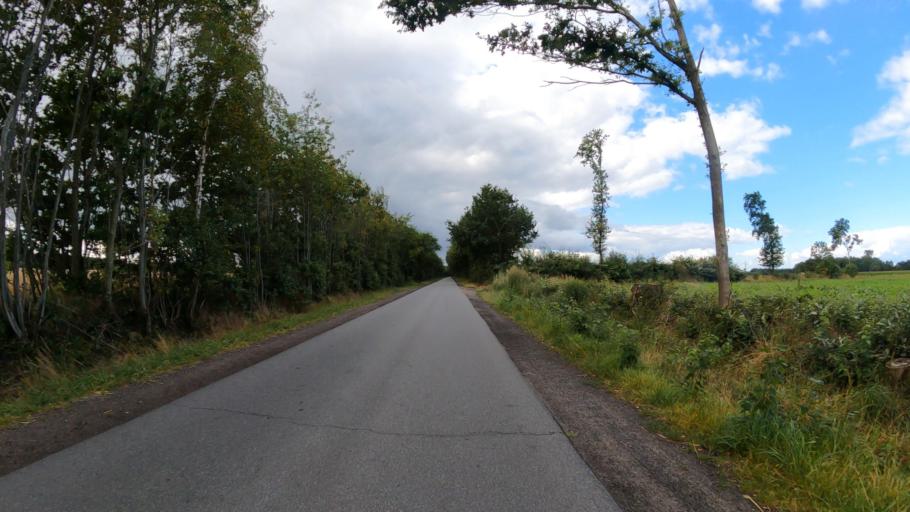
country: DE
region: Schleswig-Holstein
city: Padenstedt
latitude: 54.0300
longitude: 9.9199
